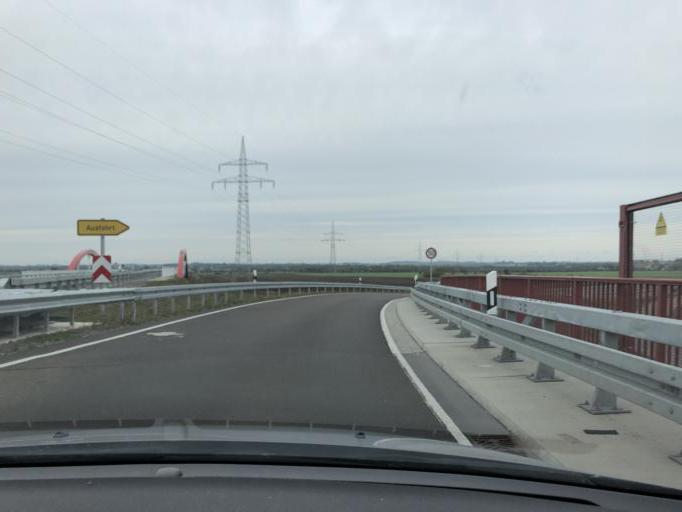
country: DE
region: Saxony-Anhalt
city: Halle (Saale)
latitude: 51.5014
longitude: 12.0167
